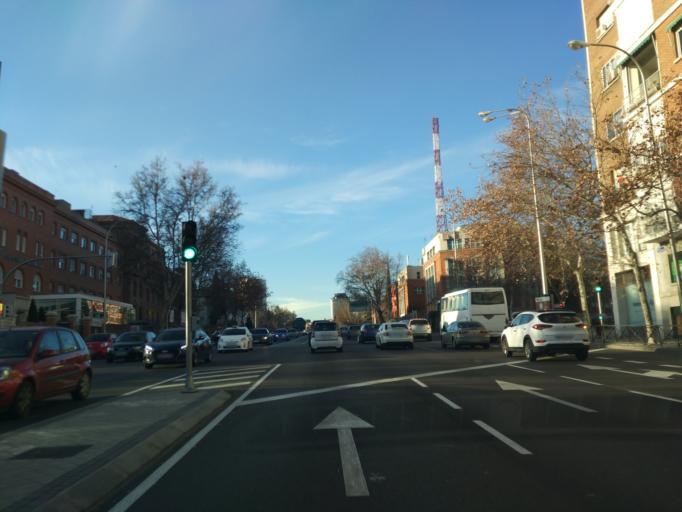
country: ES
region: Madrid
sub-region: Provincia de Madrid
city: Salamanca
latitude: 40.4423
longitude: -3.6824
